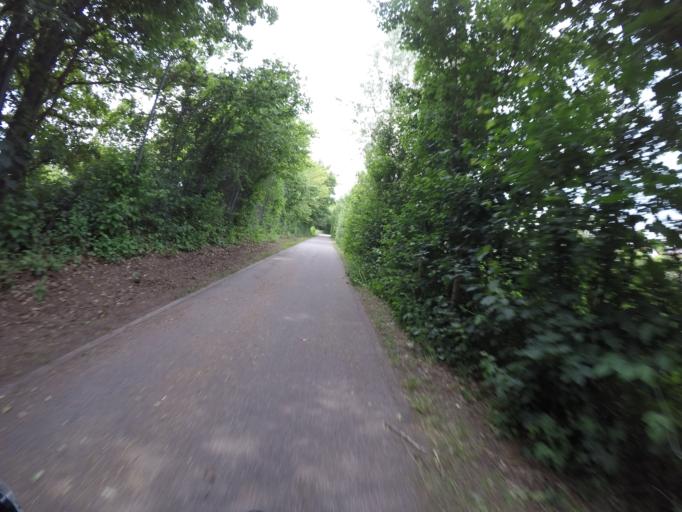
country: DE
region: Bavaria
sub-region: Lower Bavaria
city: Landshut
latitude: 48.5408
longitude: 12.1282
